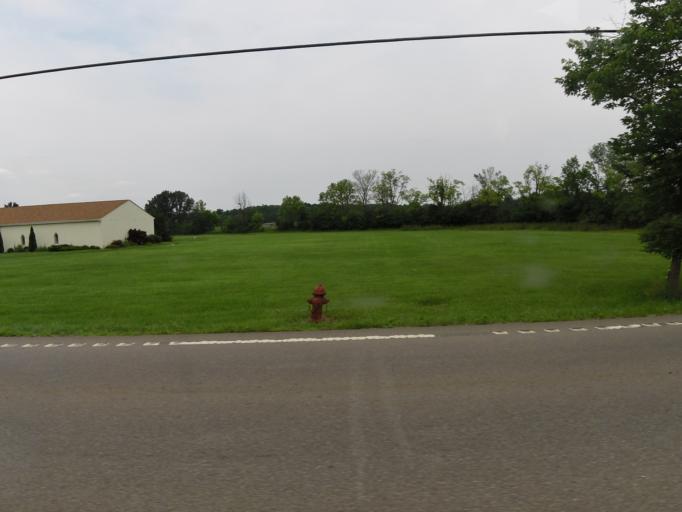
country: US
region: Ohio
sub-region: Warren County
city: Waynesville
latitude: 39.5194
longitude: -84.0559
